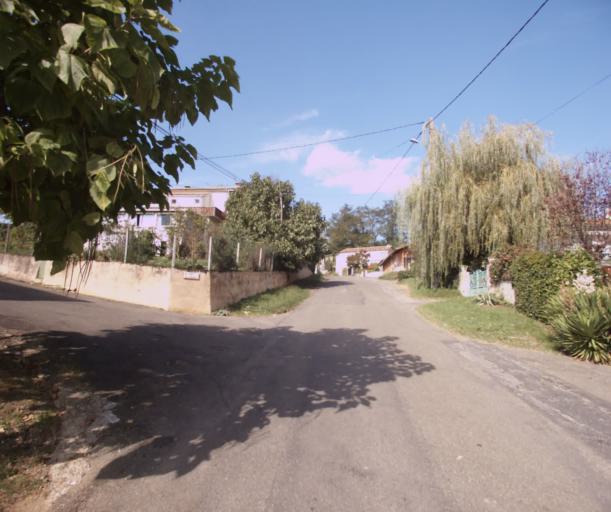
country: FR
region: Midi-Pyrenees
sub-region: Departement du Gers
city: Cazaubon
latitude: 43.9326
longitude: -0.0696
